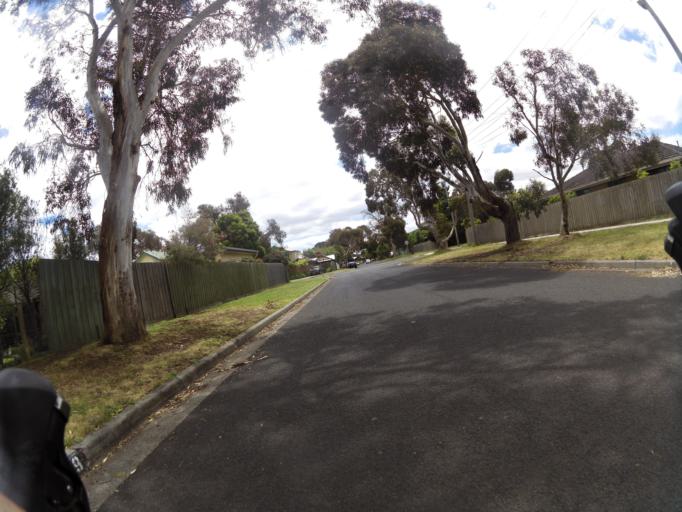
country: AU
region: Victoria
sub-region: Mornington Peninsula
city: Mornington
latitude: -38.2377
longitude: 145.0398
